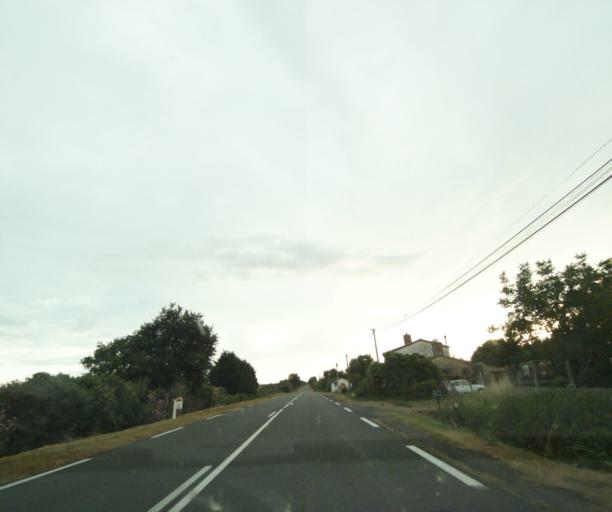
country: FR
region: Pays de la Loire
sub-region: Departement de la Vendee
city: Saint-Hilaire-de-Talmont
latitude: 46.4697
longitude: -1.5680
